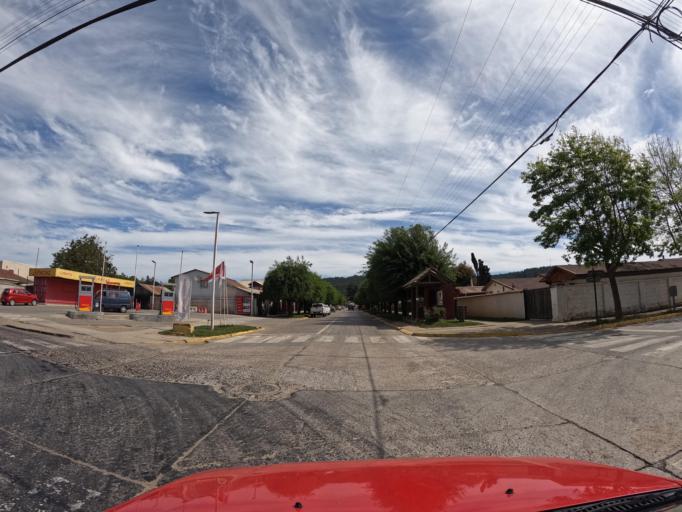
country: CL
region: Maule
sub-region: Provincia de Talca
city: Constitucion
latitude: -35.0891
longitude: -72.0209
